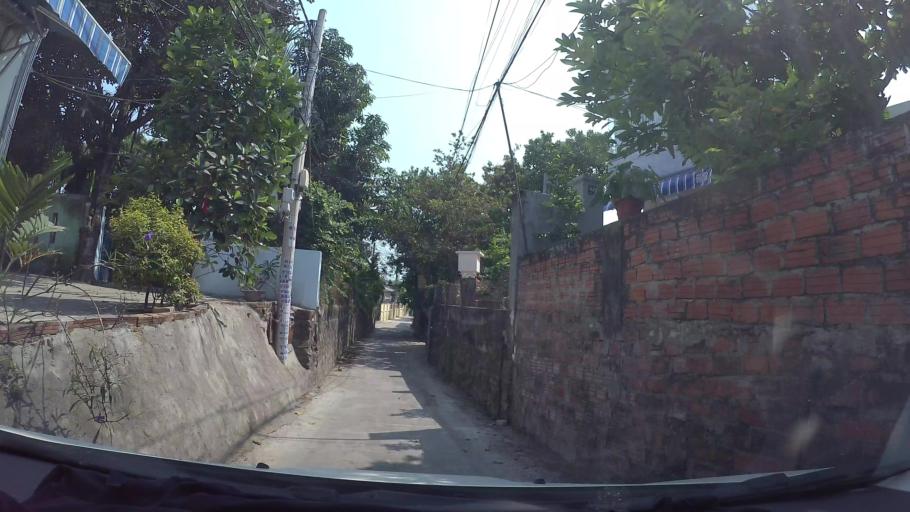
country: VN
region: Da Nang
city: Cam Le
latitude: 16.0117
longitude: 108.2018
